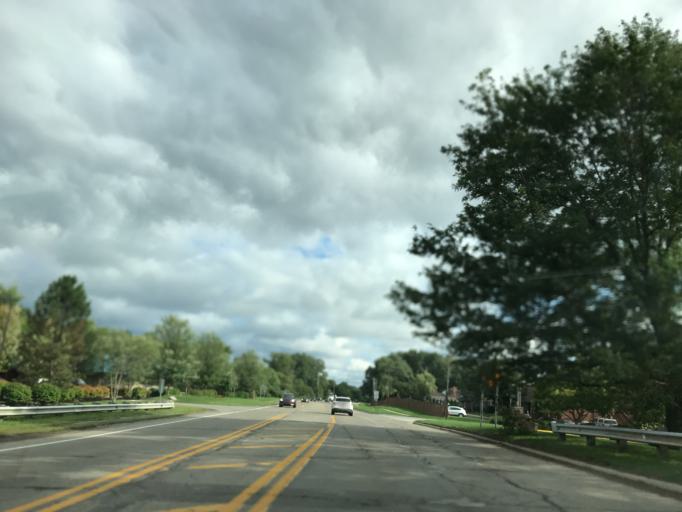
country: US
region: Michigan
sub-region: Wayne County
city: Northville
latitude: 42.4204
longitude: -83.4731
